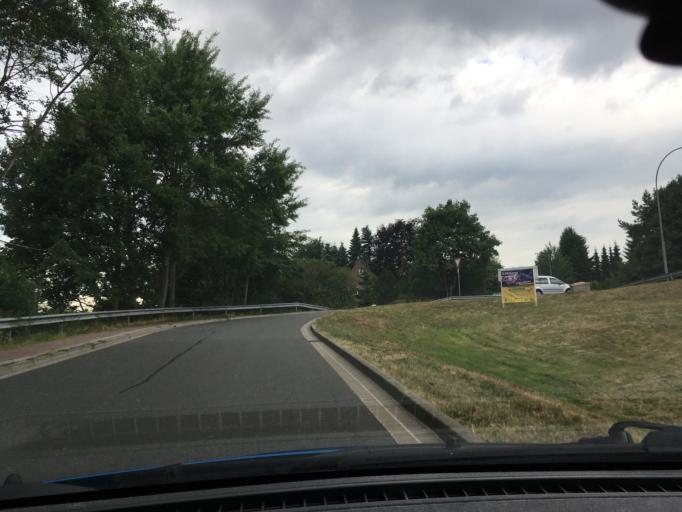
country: DE
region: Lower Saxony
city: Tostedt
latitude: 53.2755
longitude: 9.7363
